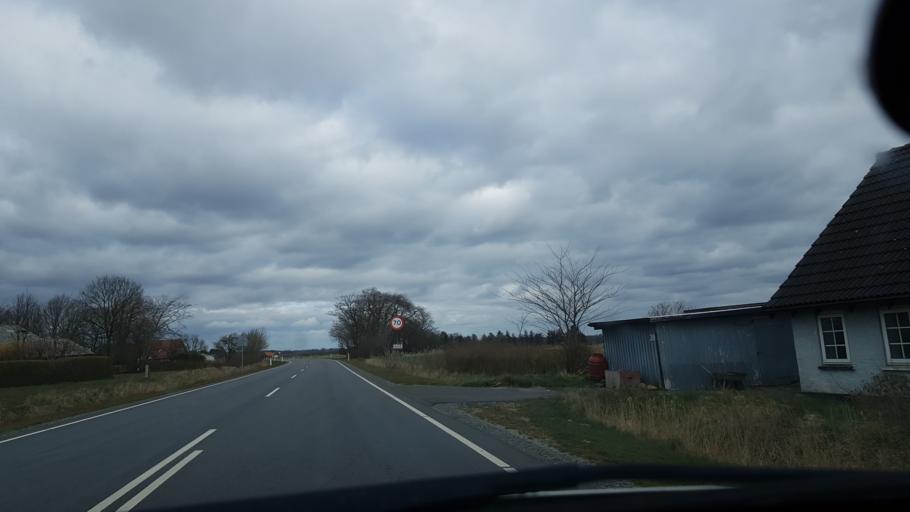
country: DK
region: South Denmark
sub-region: Vejen Kommune
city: Holsted
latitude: 55.4172
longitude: 8.8919
